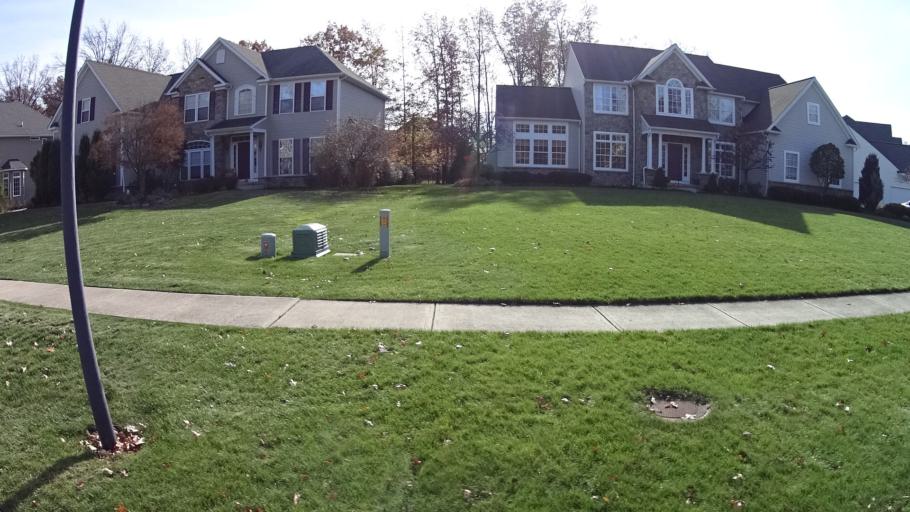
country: US
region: Ohio
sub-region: Lorain County
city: Avon Lake
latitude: 41.5017
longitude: -81.9902
